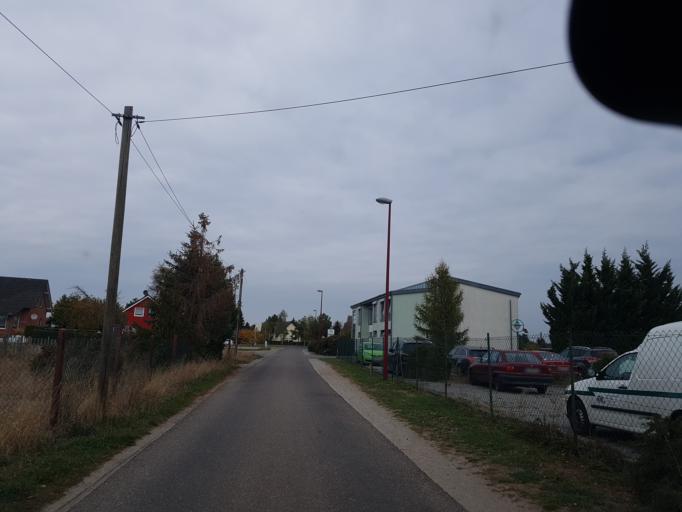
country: DE
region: Brandenburg
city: Finsterwalde
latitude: 51.6212
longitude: 13.6954
